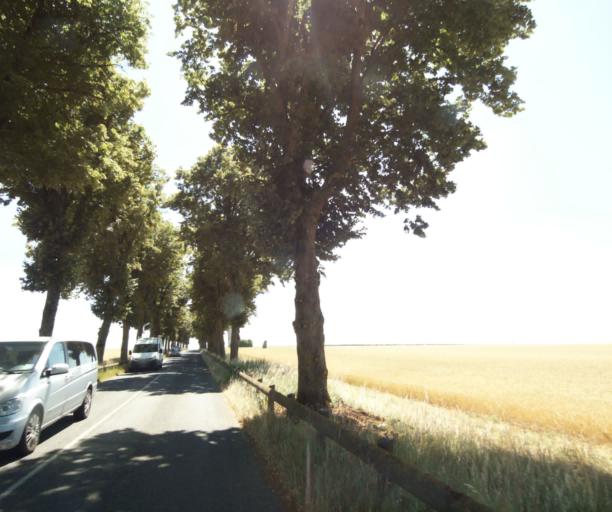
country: FR
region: Ile-de-France
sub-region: Departement de Seine-et-Marne
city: Noisy-sur-Ecole
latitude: 48.3426
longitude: 2.4583
